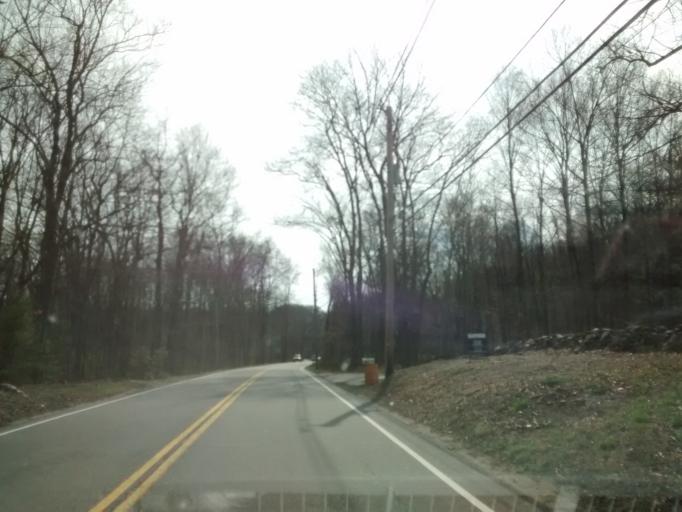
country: US
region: Massachusetts
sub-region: Worcester County
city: Sutton
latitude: 42.1573
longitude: -71.7438
